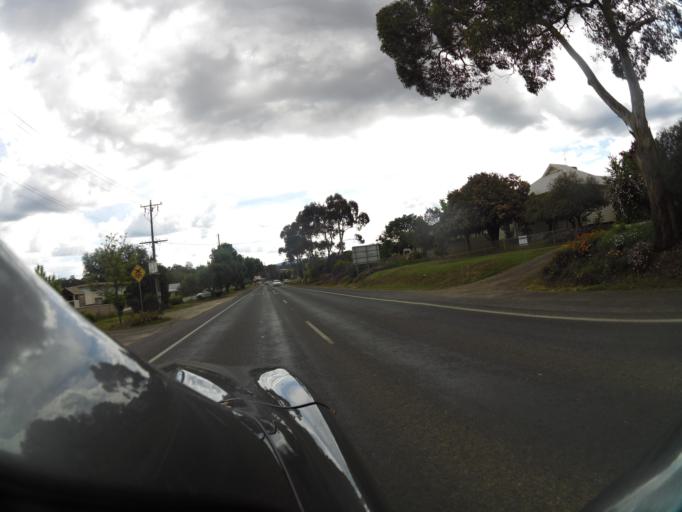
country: AU
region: Victoria
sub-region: Mount Alexander
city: Castlemaine
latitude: -37.0746
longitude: 144.2048
